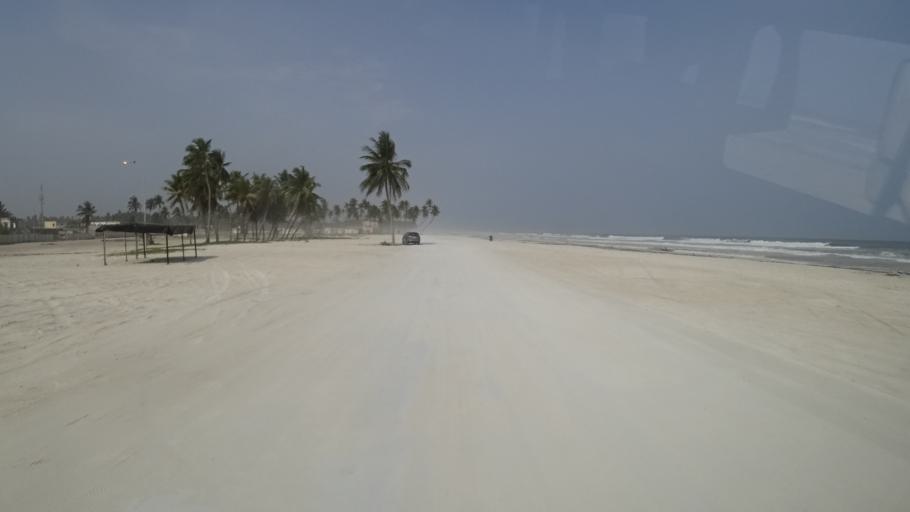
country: OM
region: Zufar
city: Salalah
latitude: 17.0006
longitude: 54.1082
